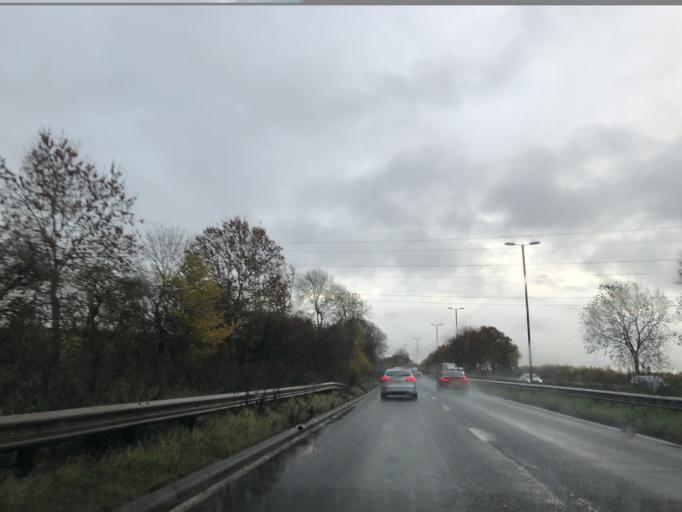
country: GB
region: England
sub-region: Solihull
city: Meriden
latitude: 52.4313
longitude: -1.5909
